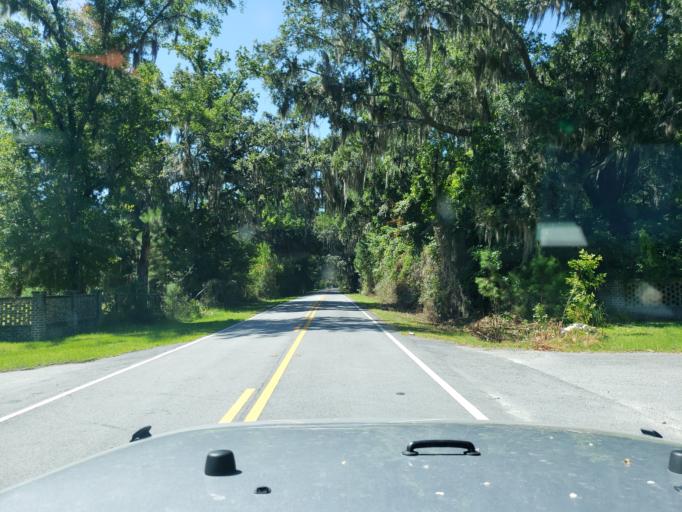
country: US
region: Georgia
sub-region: Chatham County
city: Georgetown
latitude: 31.9560
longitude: -81.2163
